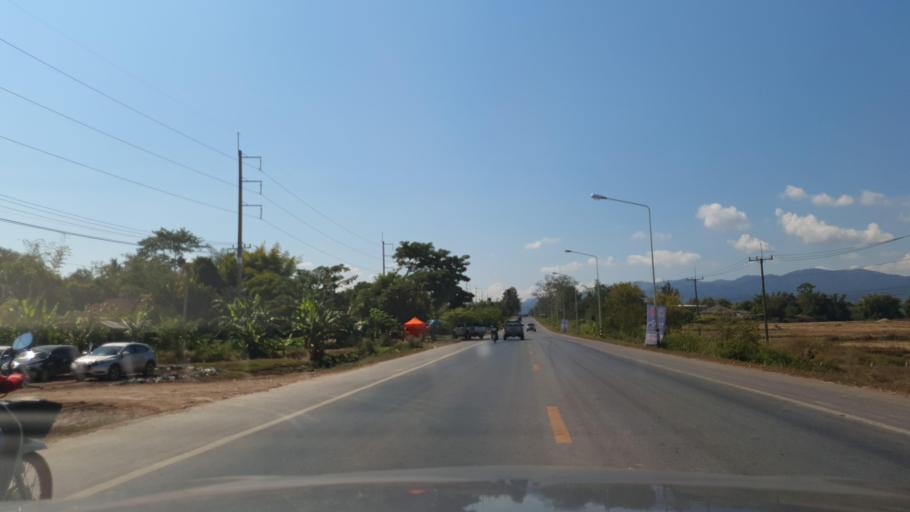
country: TH
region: Nan
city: Tha Wang Pha
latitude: 19.0233
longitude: 100.7945
